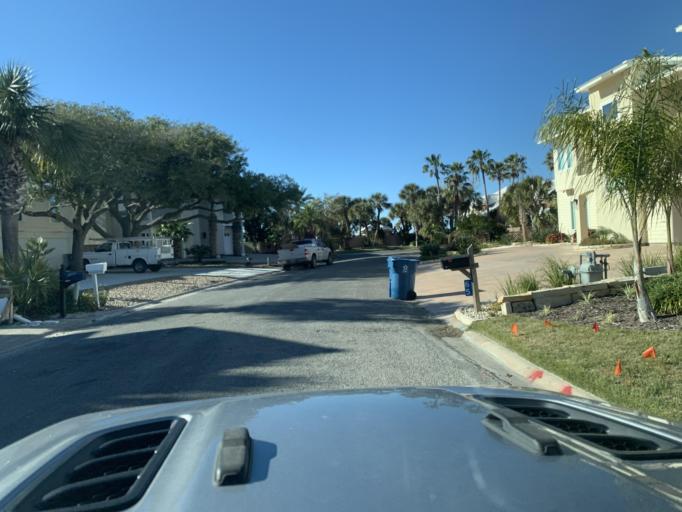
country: US
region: Texas
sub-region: Aransas County
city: Rockport
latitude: 28.0353
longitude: -97.0332
